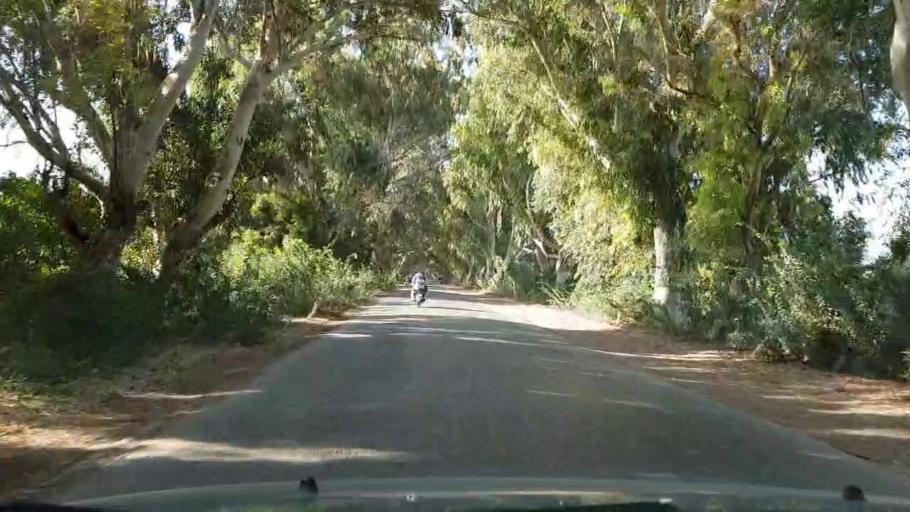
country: PK
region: Sindh
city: Tando Ghulam Ali
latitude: 25.1328
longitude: 68.8820
